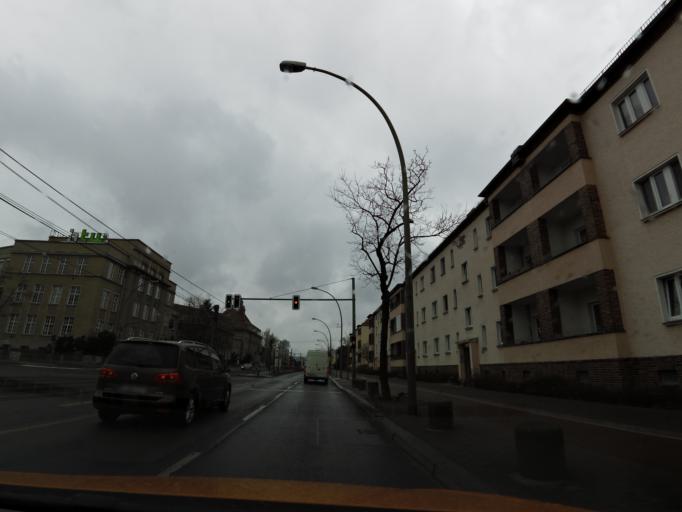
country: DE
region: Berlin
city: Karlshorst
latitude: 52.4920
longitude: 13.5274
